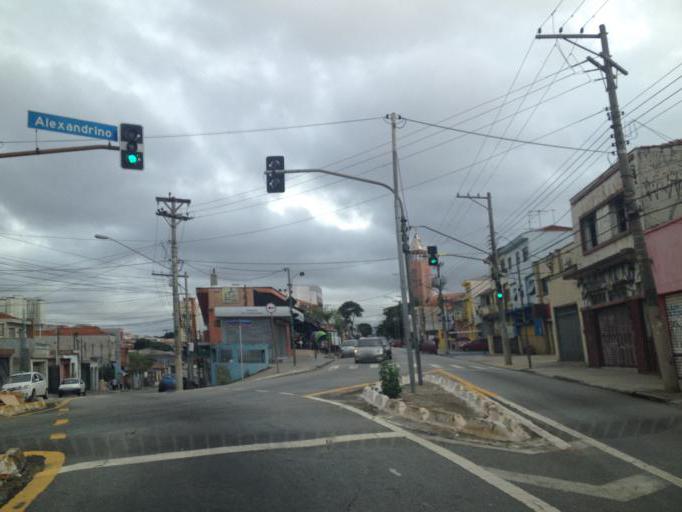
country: BR
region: Sao Paulo
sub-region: Sao Caetano Do Sul
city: Sao Caetano do Sul
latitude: -23.5659
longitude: -46.5696
